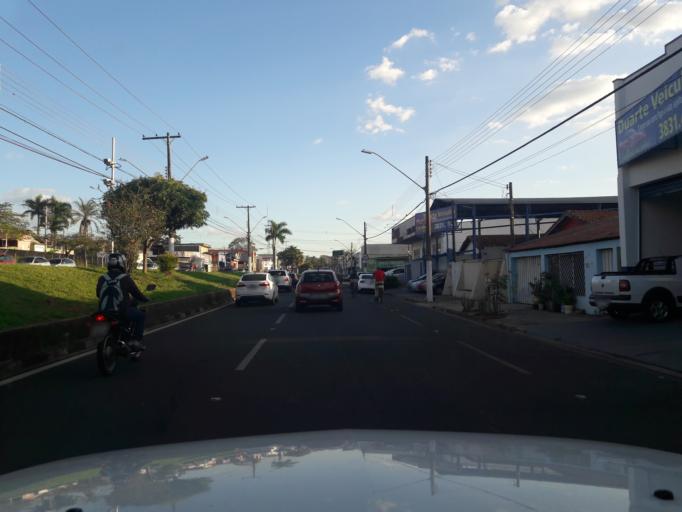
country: BR
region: Sao Paulo
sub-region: Moji-Guacu
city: Mogi-Gaucu
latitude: -22.3930
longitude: -46.9460
